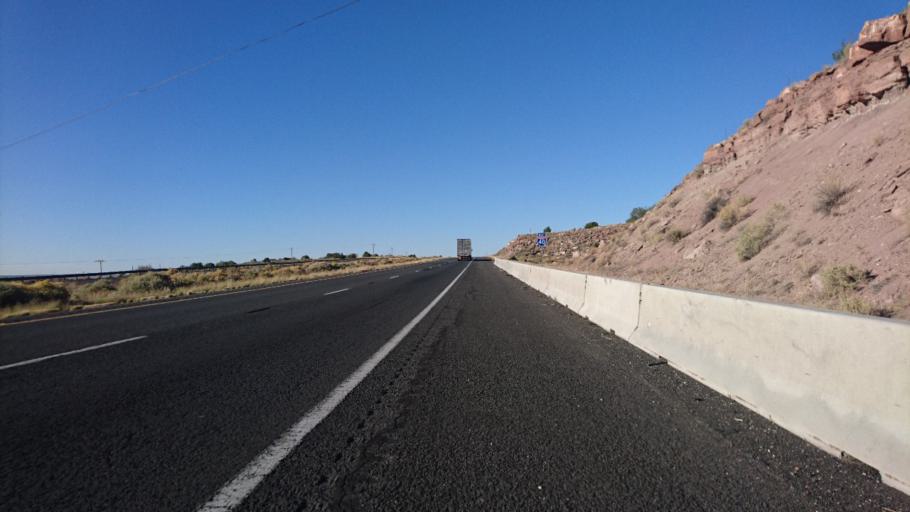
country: US
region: Arizona
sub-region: Apache County
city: Houck
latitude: 35.1614
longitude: -109.4914
